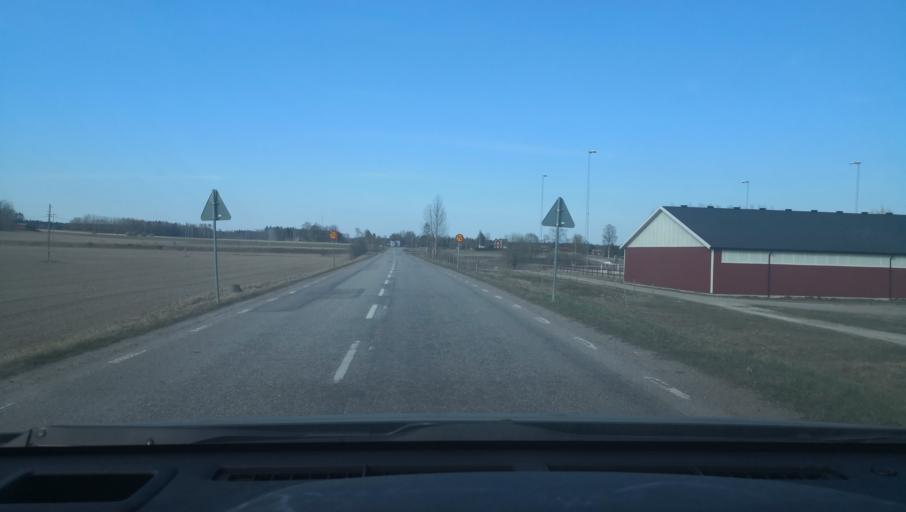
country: SE
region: Uppsala
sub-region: Heby Kommun
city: Heby
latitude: 59.9471
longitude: 16.8684
